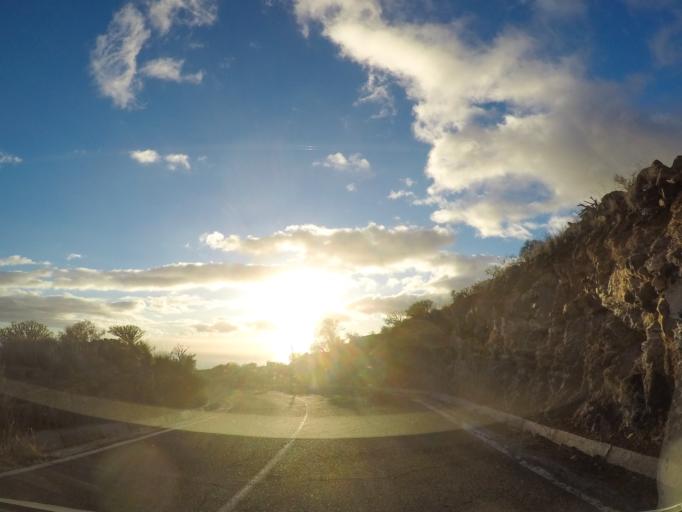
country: ES
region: Canary Islands
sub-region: Provincia de Santa Cruz de Tenerife
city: Alajero
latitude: 28.0403
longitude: -17.2330
